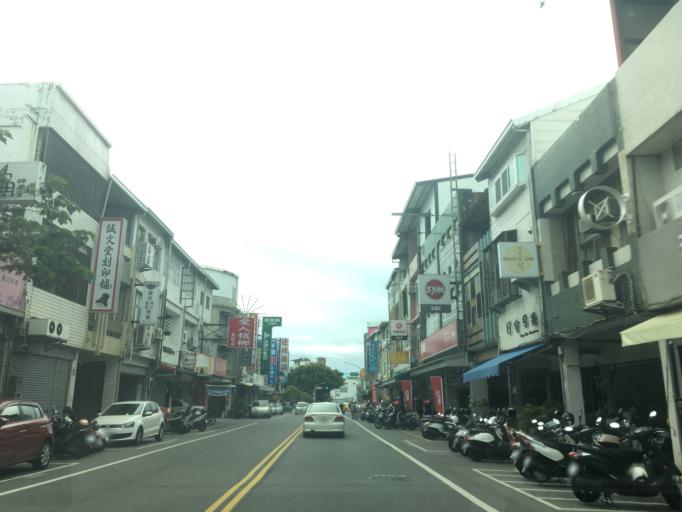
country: TW
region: Taiwan
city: Taitung City
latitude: 22.7580
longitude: 121.1420
